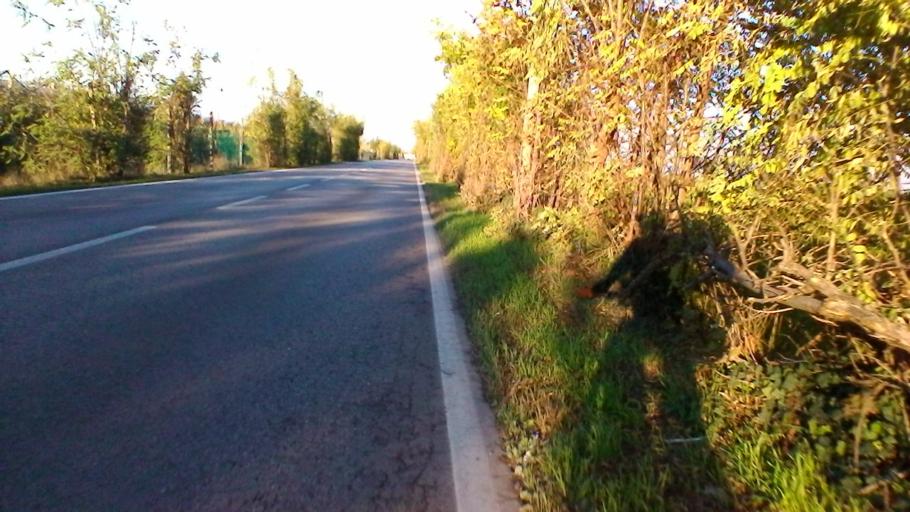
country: IT
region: Veneto
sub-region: Provincia di Verona
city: Alpo
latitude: 45.3609
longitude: 10.9049
